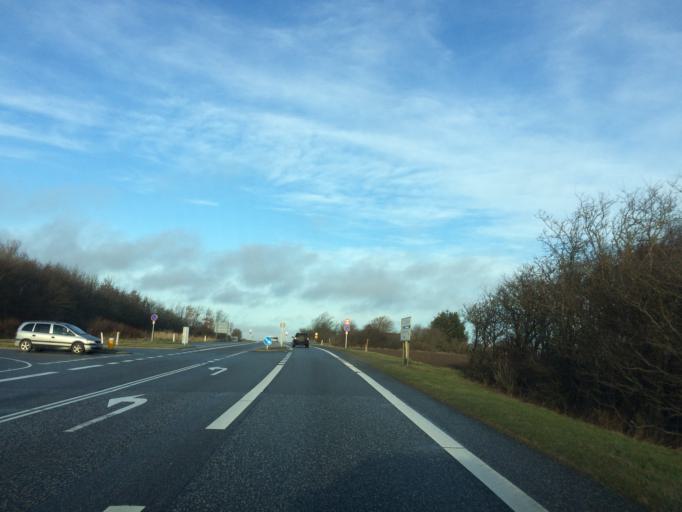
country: DK
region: North Denmark
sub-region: Thisted Kommune
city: Thisted
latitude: 56.8826
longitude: 8.5950
